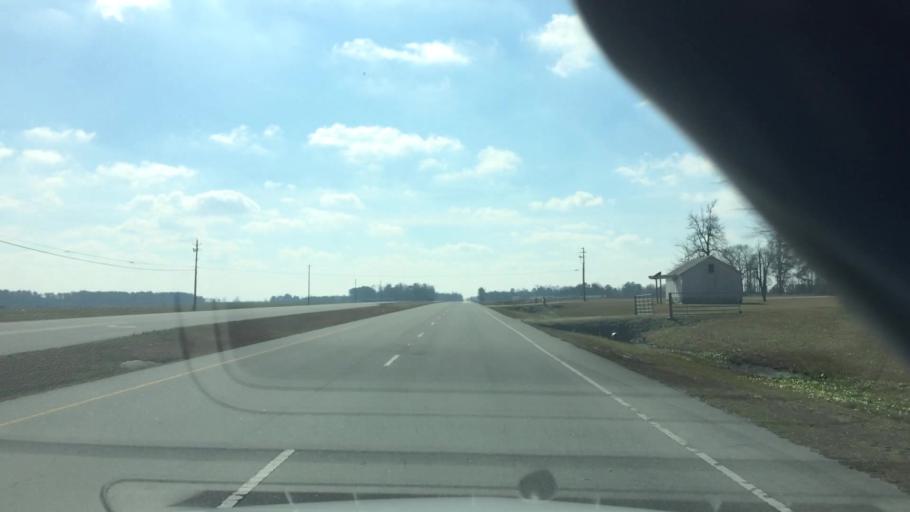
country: US
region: North Carolina
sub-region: Duplin County
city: Beulaville
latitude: 35.1024
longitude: -77.7228
